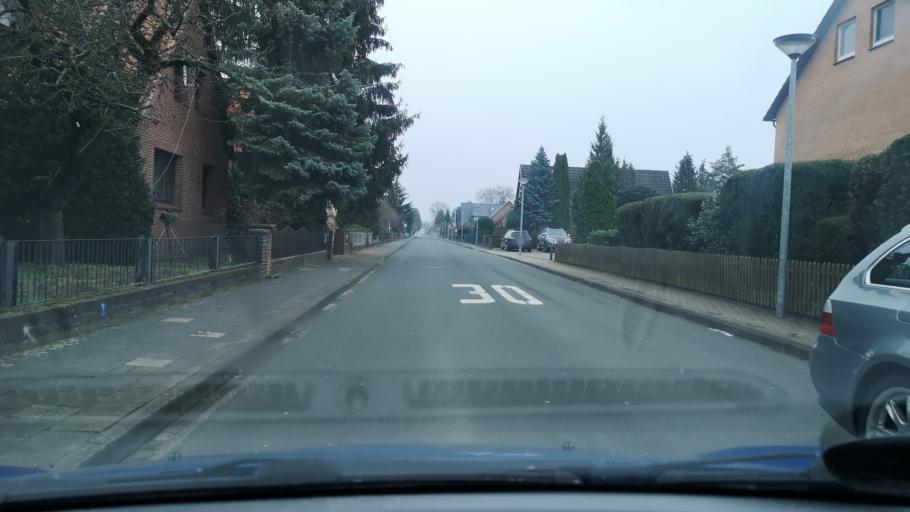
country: DE
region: Lower Saxony
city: Celle
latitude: 52.6045
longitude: 10.0615
